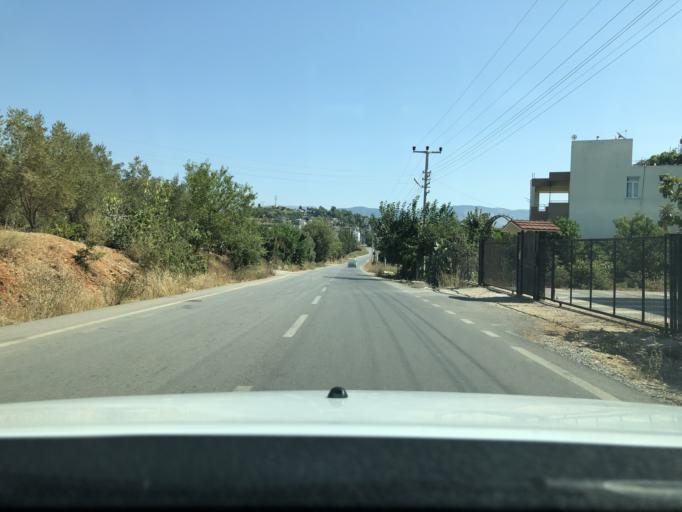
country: TR
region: Antalya
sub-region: Manavgat
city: Manavgat
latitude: 36.8057
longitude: 31.4781
